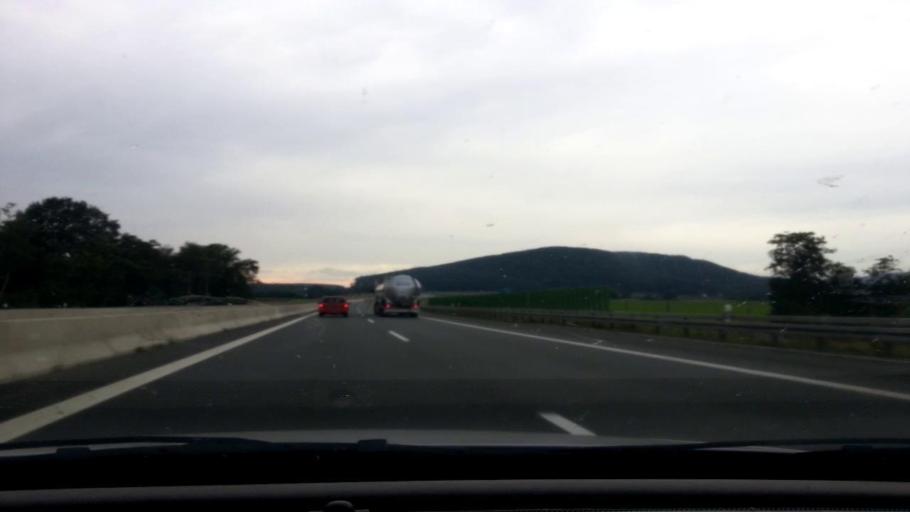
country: DE
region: Bavaria
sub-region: Upper Franconia
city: Harsdorf
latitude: 50.0335
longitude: 11.5503
